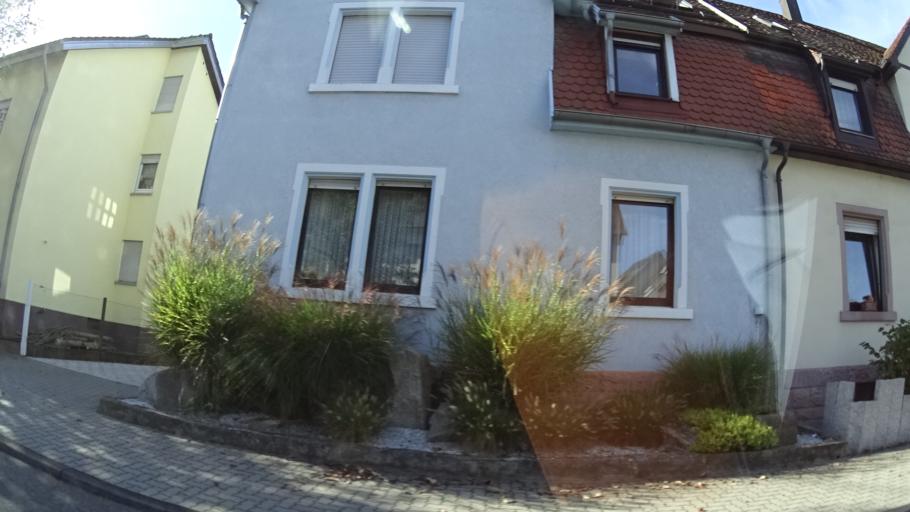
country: DE
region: Baden-Wuerttemberg
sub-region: Karlsruhe Region
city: Weingarten
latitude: 49.0128
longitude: 8.4944
